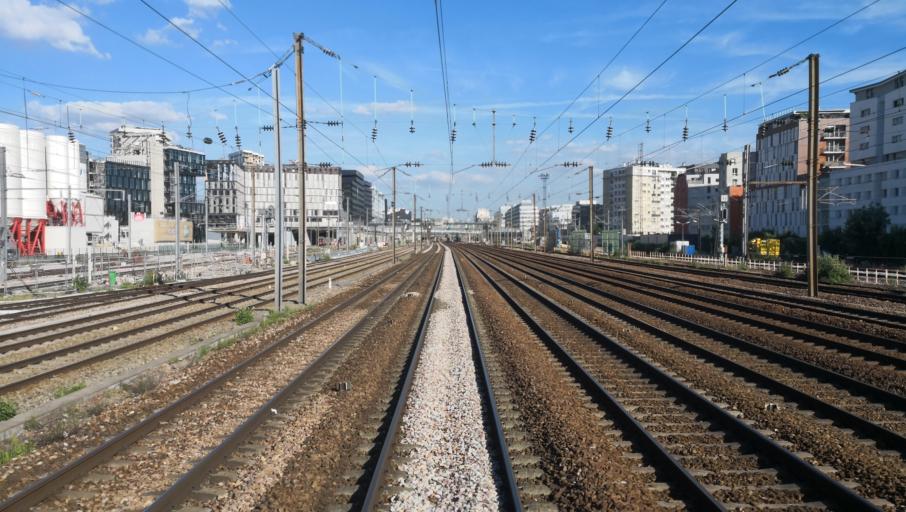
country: FR
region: Ile-de-France
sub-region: Departement des Hauts-de-Seine
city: Clichy
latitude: 48.8931
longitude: 2.3055
